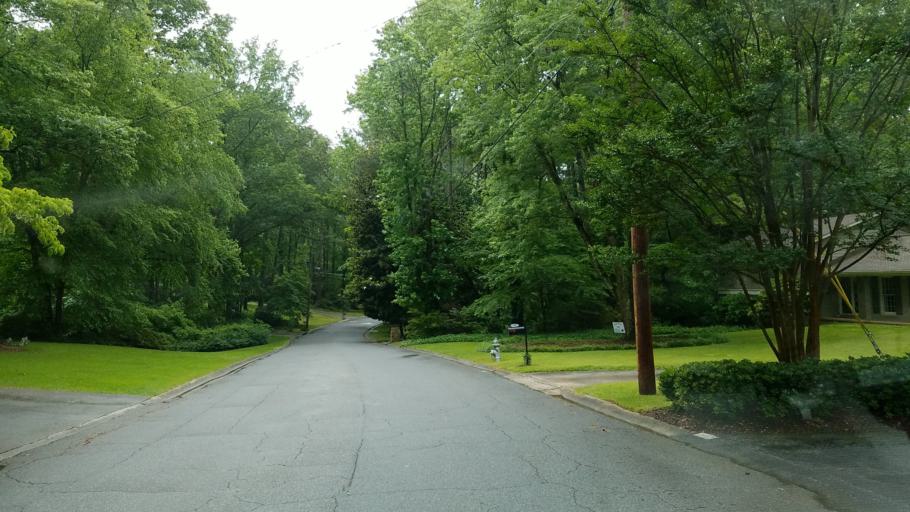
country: US
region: Georgia
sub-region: DeKalb County
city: Dunwoody
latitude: 33.9579
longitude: -84.3494
